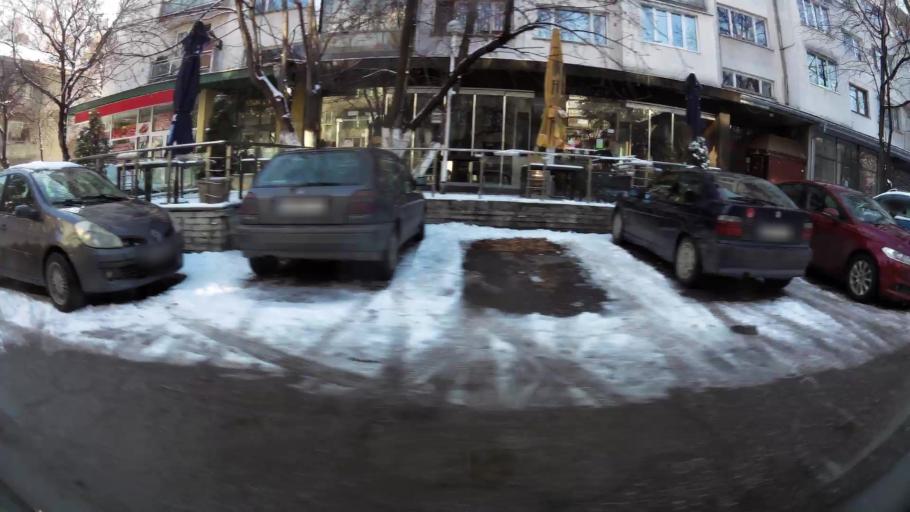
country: BG
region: Sofia-Capital
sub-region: Stolichna Obshtina
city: Sofia
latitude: 42.6703
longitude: 23.3587
